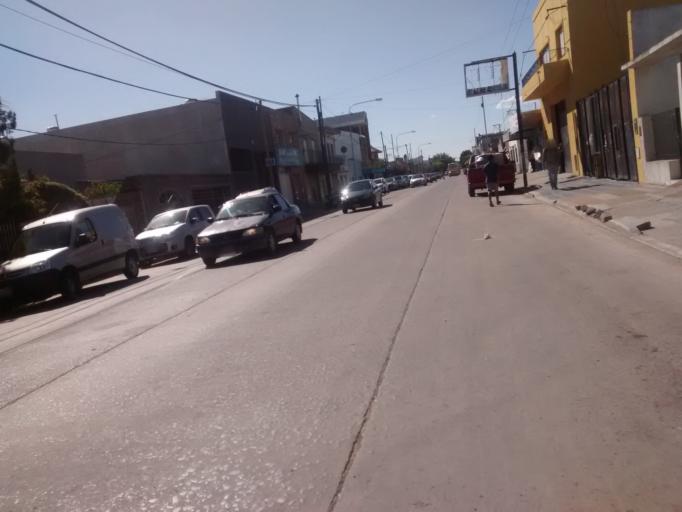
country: AR
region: Buenos Aires
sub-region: Partido de La Plata
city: La Plata
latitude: -34.9229
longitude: -57.9060
